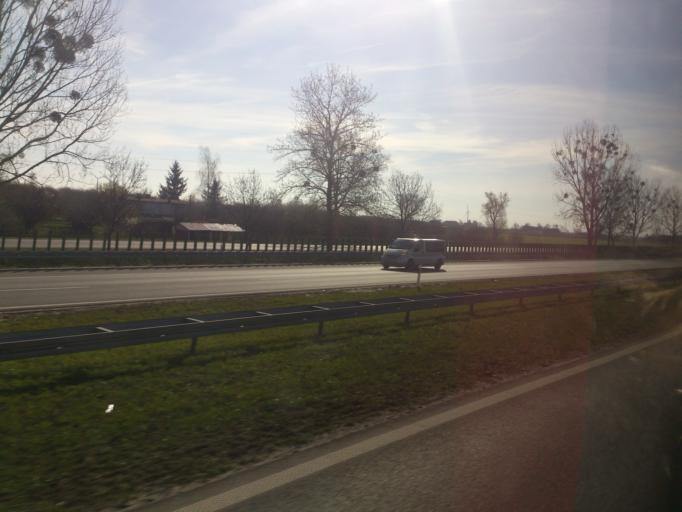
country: PL
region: Kujawsko-Pomorskie
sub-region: Powiat aleksandrowski
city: Raciazek
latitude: 52.8396
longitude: 18.7939
